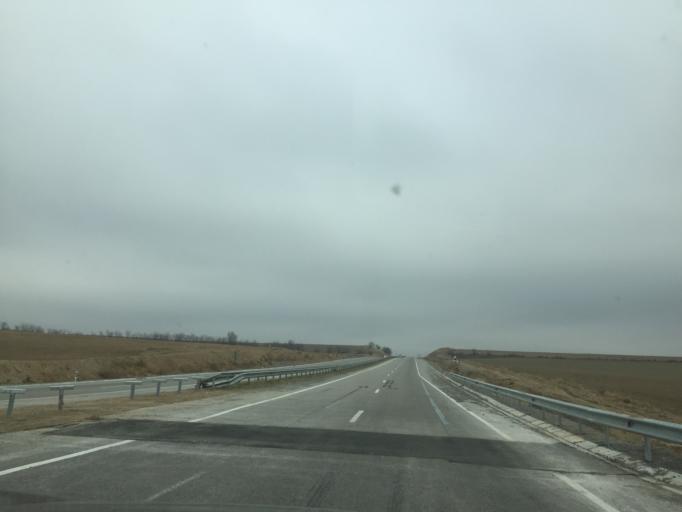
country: KZ
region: Ongtustik Qazaqstan
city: Aksu
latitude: 42.4763
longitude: 69.8875
